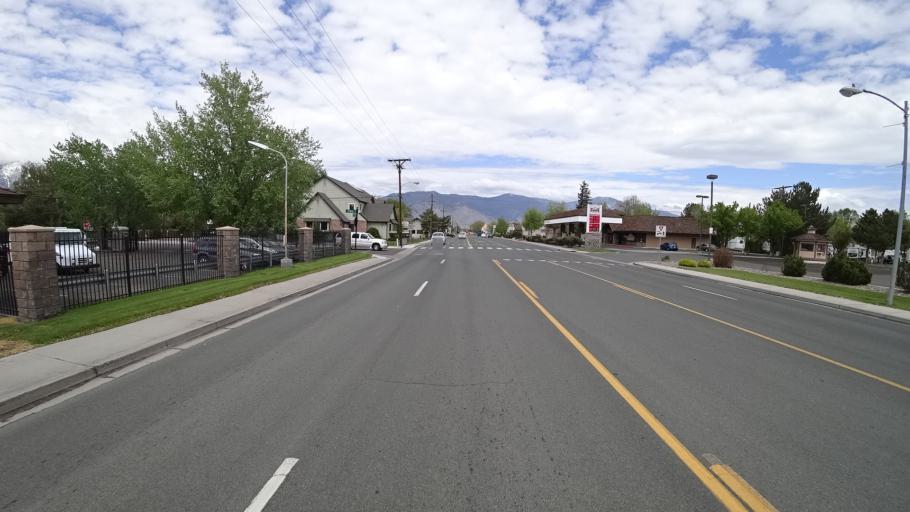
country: US
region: Nevada
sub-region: Douglas County
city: Minden
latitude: 38.9564
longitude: -119.7694
